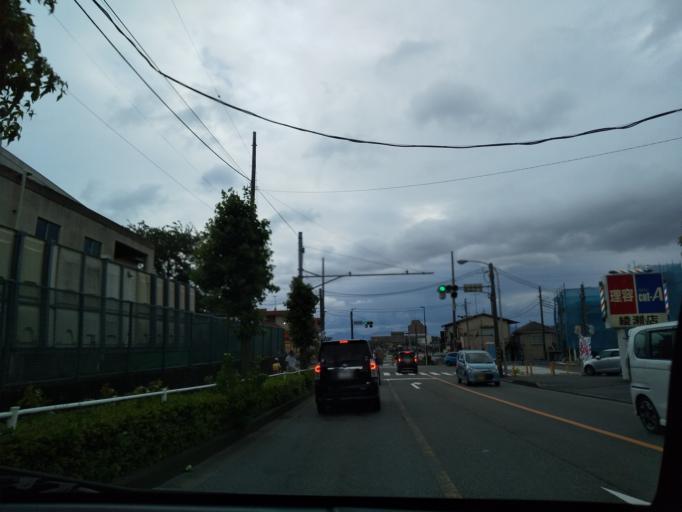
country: JP
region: Kanagawa
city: Minami-rinkan
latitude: 35.4394
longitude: 139.4329
